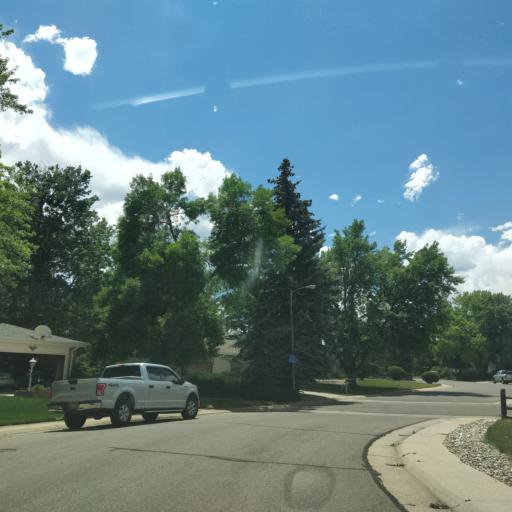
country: US
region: Colorado
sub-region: Jefferson County
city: Lakewood
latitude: 39.6843
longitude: -105.0952
